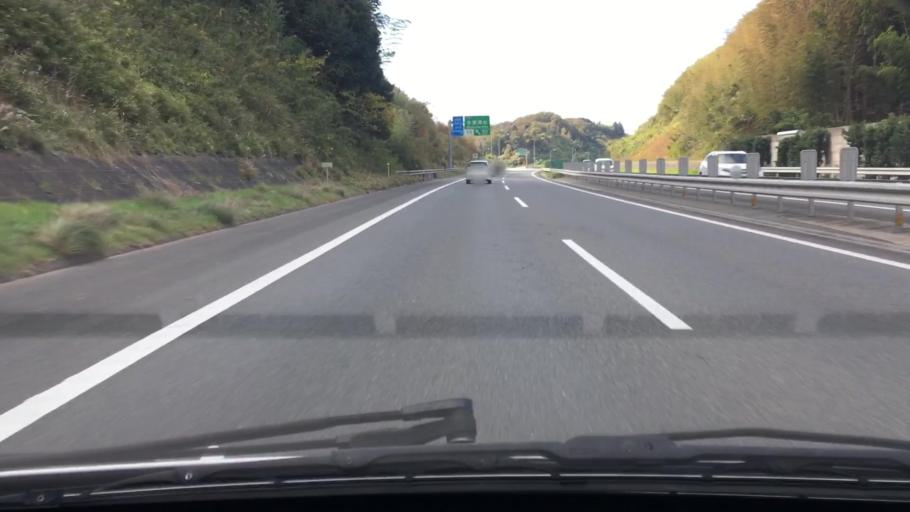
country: JP
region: Chiba
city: Kisarazu
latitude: 35.3888
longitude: 140.0010
